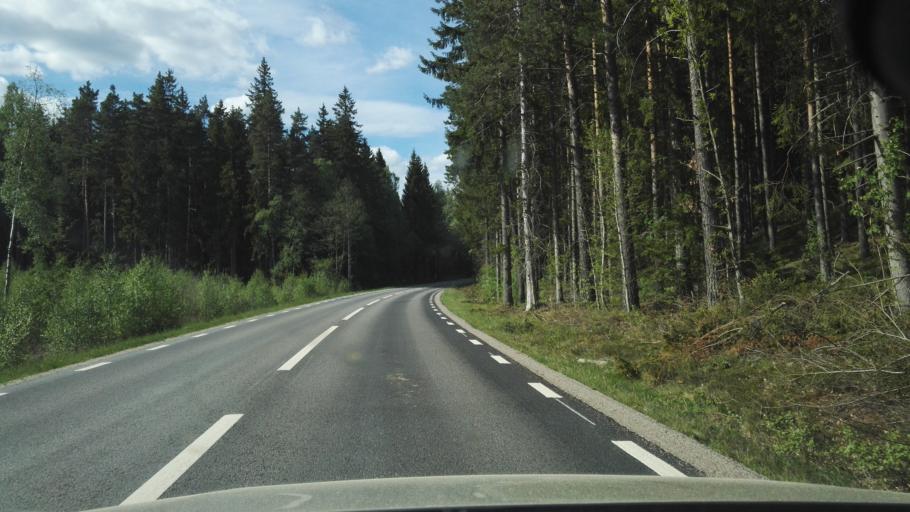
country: SE
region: Kronoberg
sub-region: Vaxjo Kommun
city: Braas
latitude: 57.1449
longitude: 14.9597
